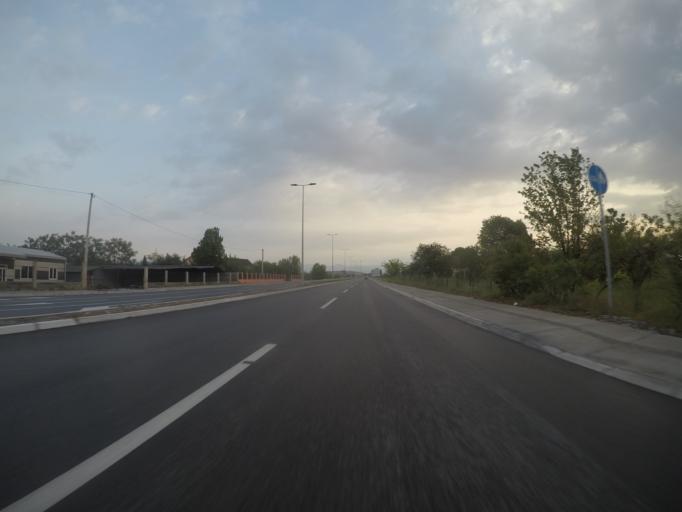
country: ME
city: Mojanovici
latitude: 42.3521
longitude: 19.2227
